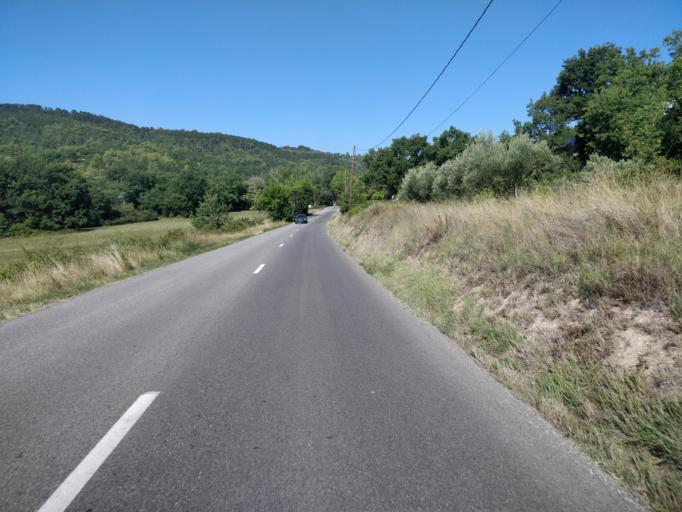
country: FR
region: Provence-Alpes-Cote d'Azur
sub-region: Departement des Alpes-de-Haute-Provence
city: Riez
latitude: 43.8428
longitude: 6.2109
